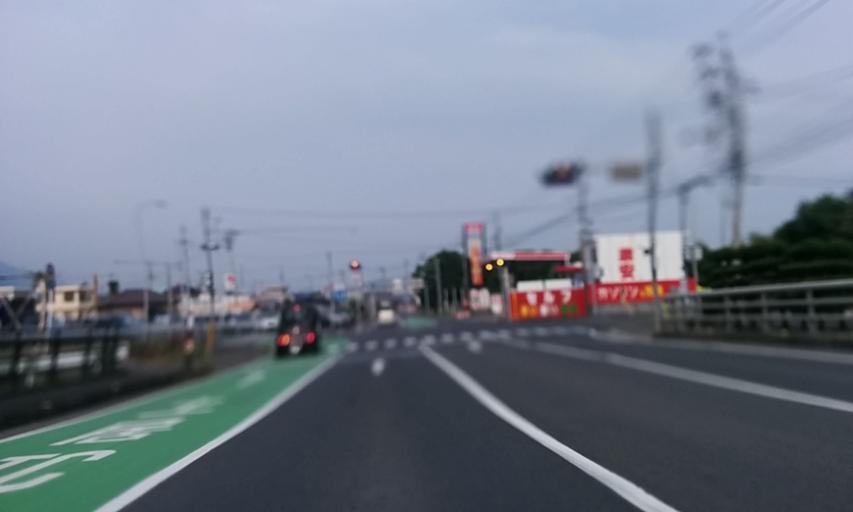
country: JP
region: Ehime
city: Kawanoecho
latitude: 33.9651
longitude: 133.4690
